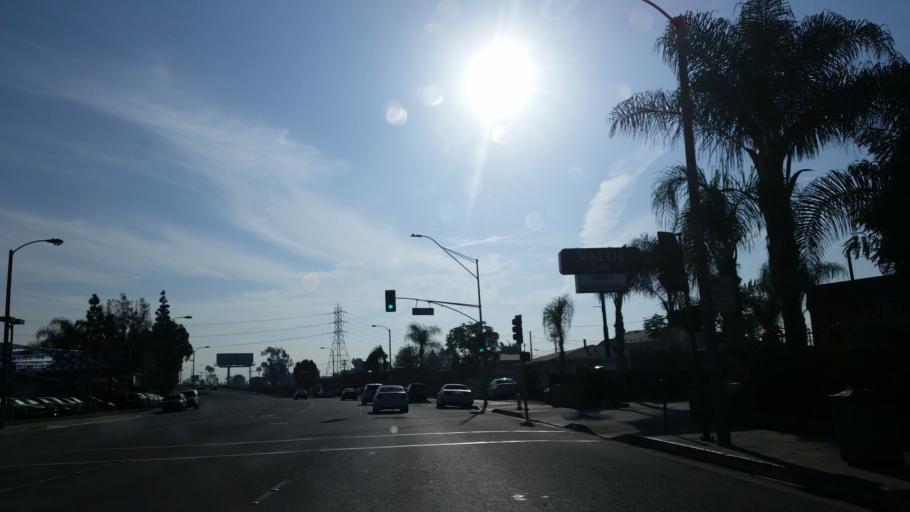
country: US
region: California
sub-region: Los Angeles County
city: Bellflower
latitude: 33.8884
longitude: -118.1134
